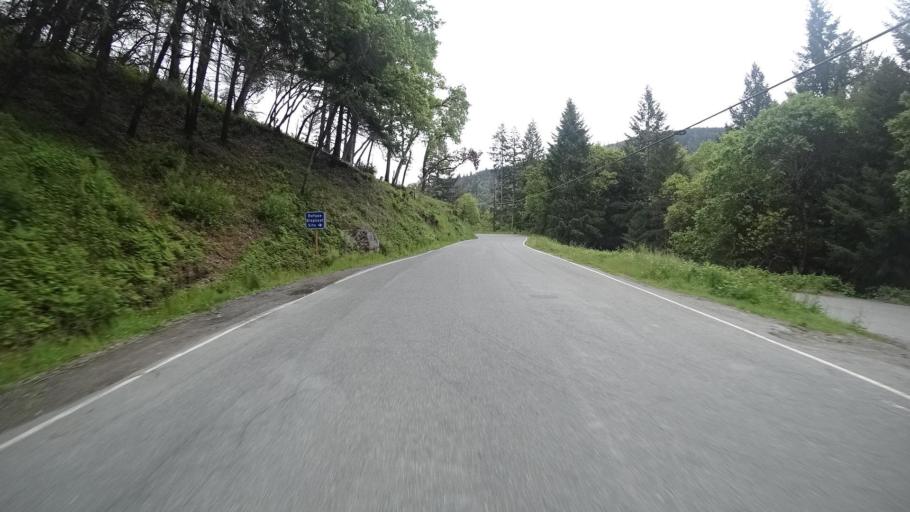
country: US
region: California
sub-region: Humboldt County
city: Willow Creek
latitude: 41.1986
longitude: -123.7448
